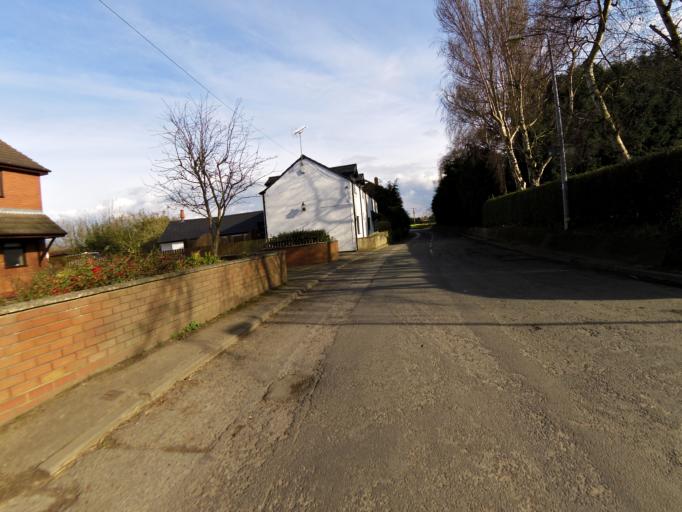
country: GB
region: England
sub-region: East Riding of Yorkshire
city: Pollington
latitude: 53.6946
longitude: -1.0582
